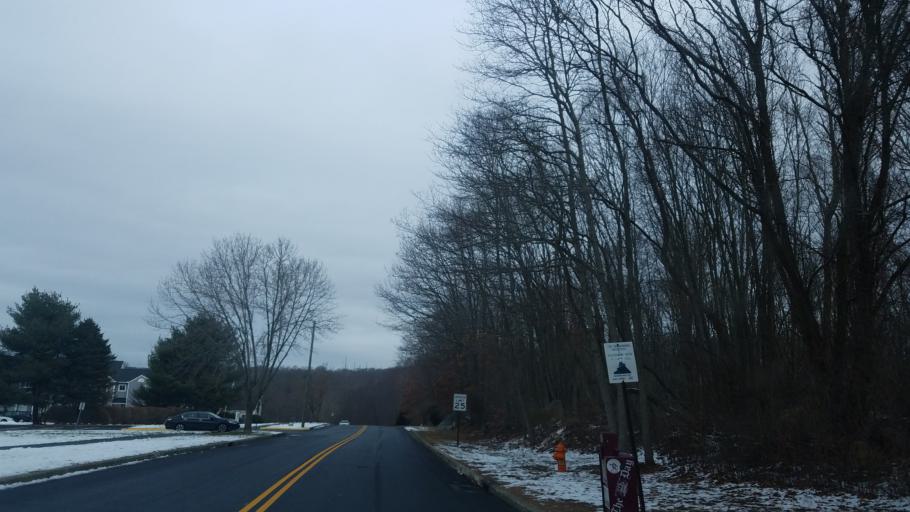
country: US
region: Connecticut
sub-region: New London County
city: Central Waterford
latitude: 41.3476
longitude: -72.1570
